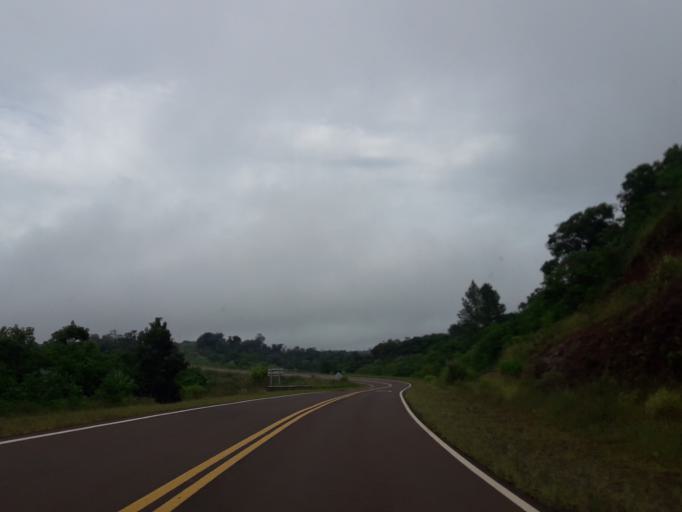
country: AR
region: Misiones
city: Bernardo de Irigoyen
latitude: -26.4019
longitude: -53.8194
